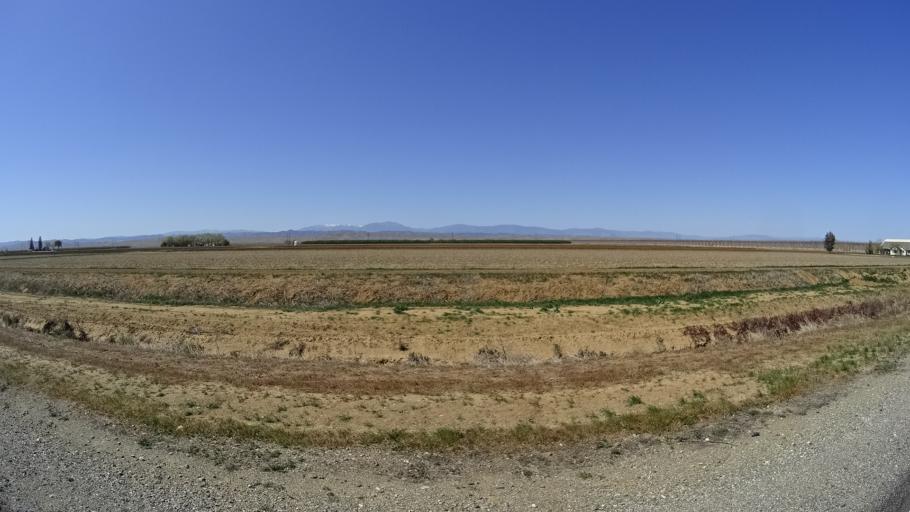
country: US
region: California
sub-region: Glenn County
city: Willows
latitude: 39.4704
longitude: -122.2488
